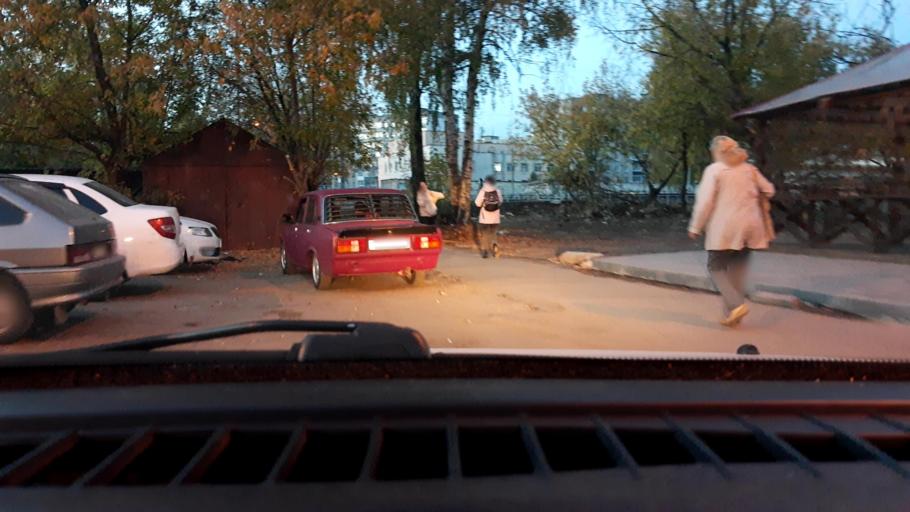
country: RU
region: Nizjnij Novgorod
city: Neklyudovo
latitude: 56.3559
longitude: 43.8575
